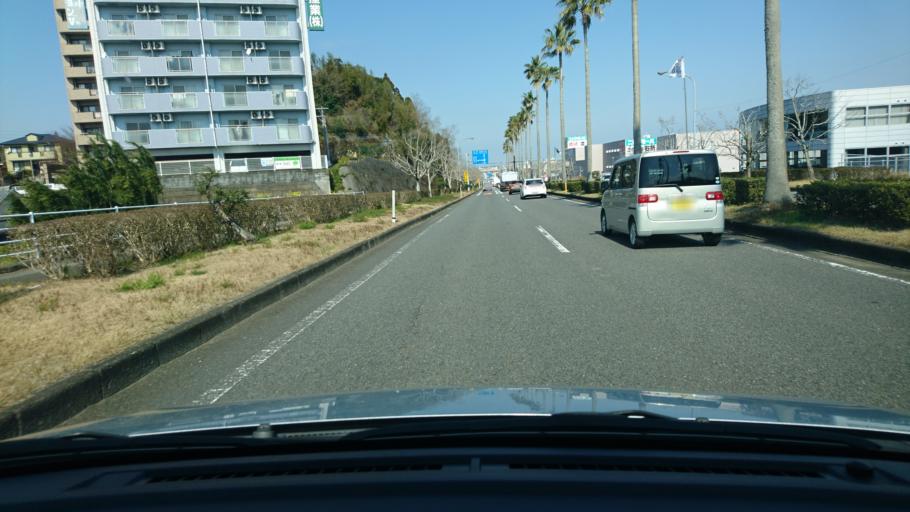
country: JP
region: Miyazaki
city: Miyazaki-shi
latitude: 31.8835
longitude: 131.4111
